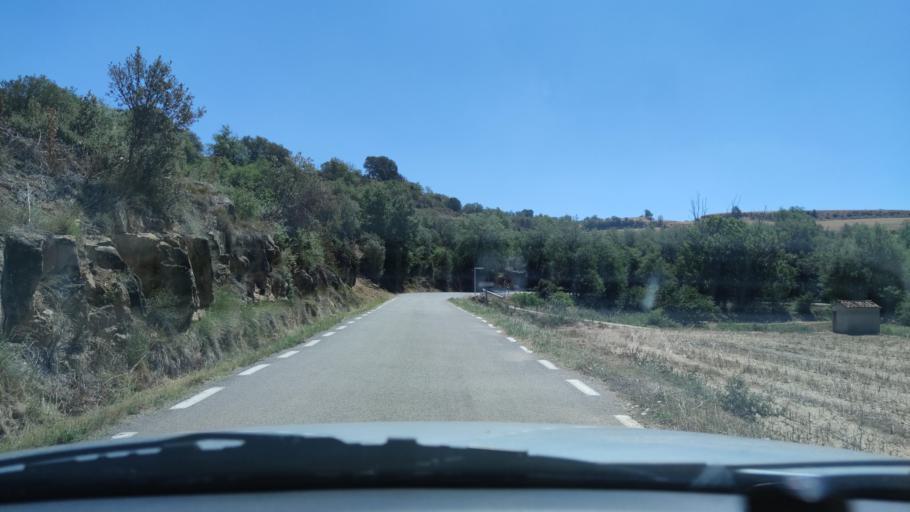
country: ES
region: Catalonia
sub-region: Provincia de Lleida
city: Tora de Riubregos
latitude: 41.8375
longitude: 1.4227
